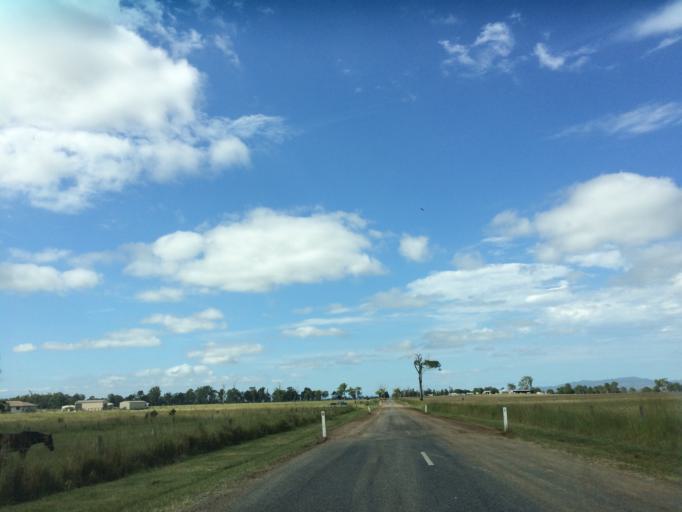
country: AU
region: Queensland
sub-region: Logan
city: Cedar Vale
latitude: -27.8707
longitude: 152.9571
